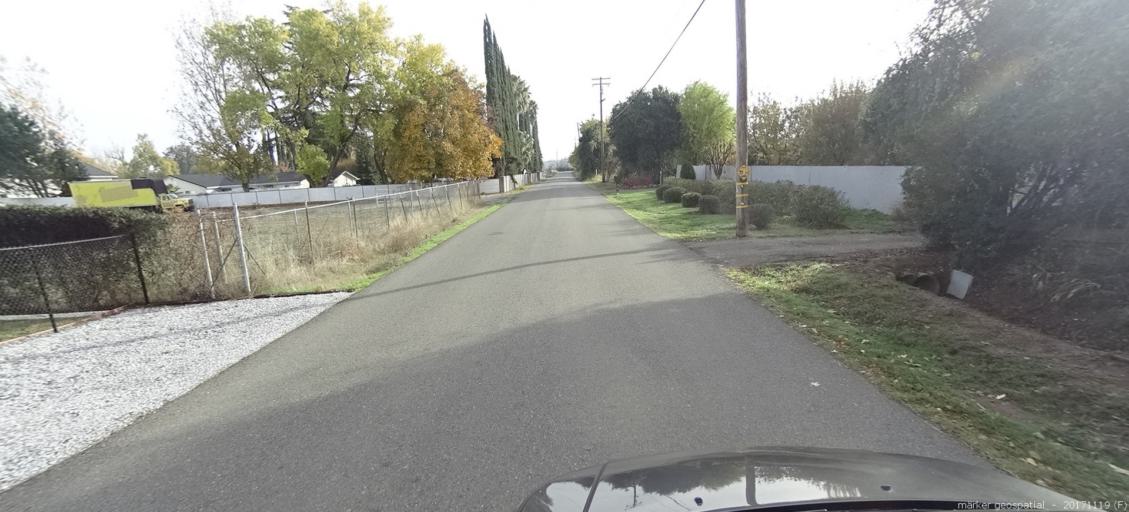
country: US
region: California
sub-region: Shasta County
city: Anderson
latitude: 40.5148
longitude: -122.3373
